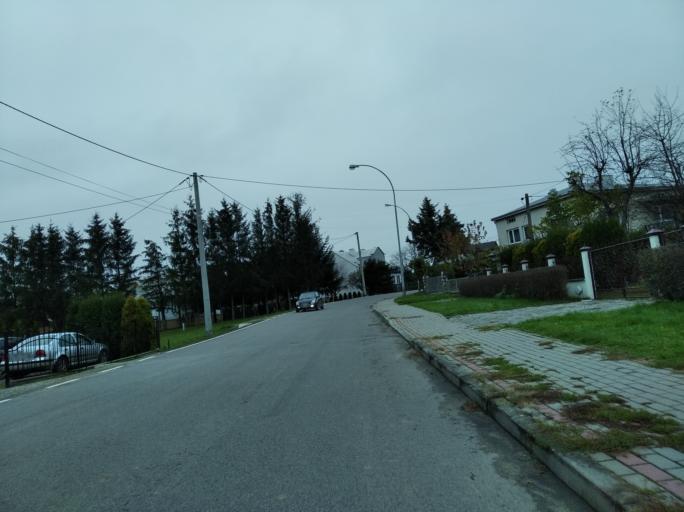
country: PL
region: Subcarpathian Voivodeship
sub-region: Powiat krosnienski
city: Jedlicze
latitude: 49.7217
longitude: 21.6508
